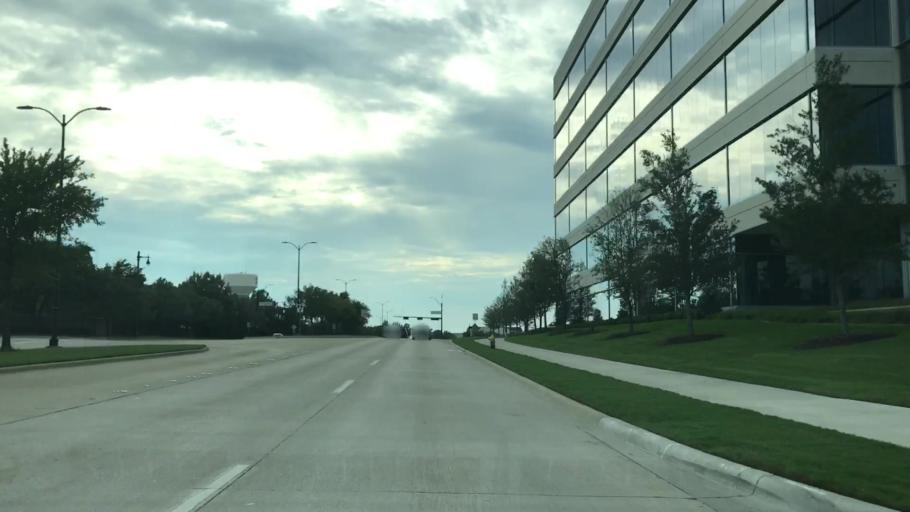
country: US
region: Texas
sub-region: Collin County
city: Frisco
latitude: 33.1069
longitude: -96.8326
